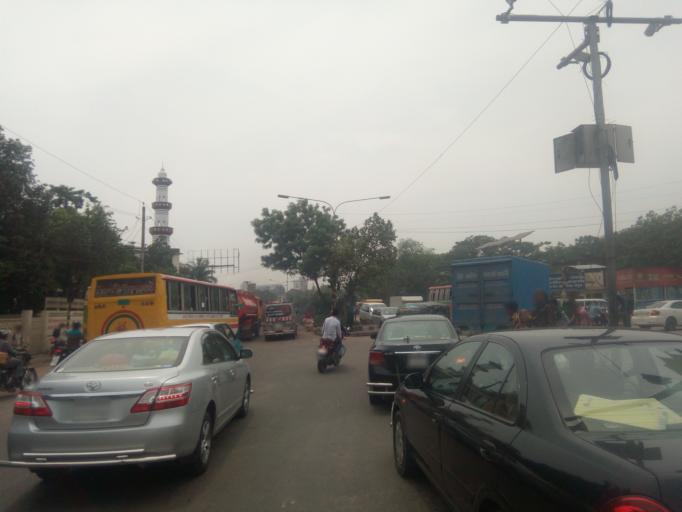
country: BD
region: Dhaka
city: Azimpur
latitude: 23.7815
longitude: 90.3519
